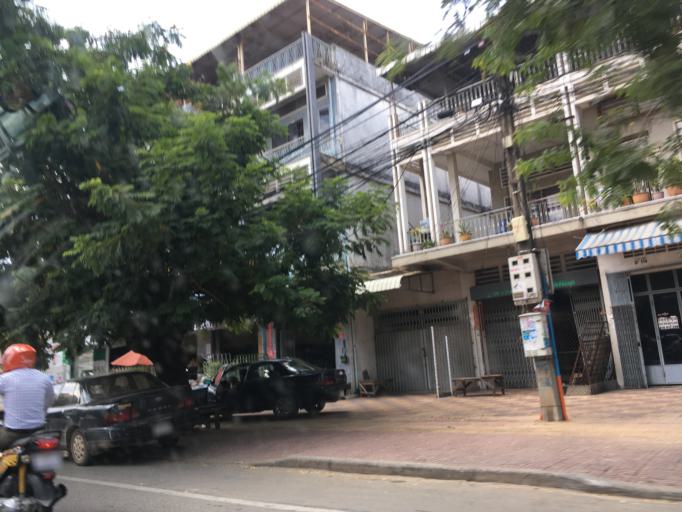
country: KH
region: Phnom Penh
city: Phnom Penh
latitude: 11.5439
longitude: 104.9147
